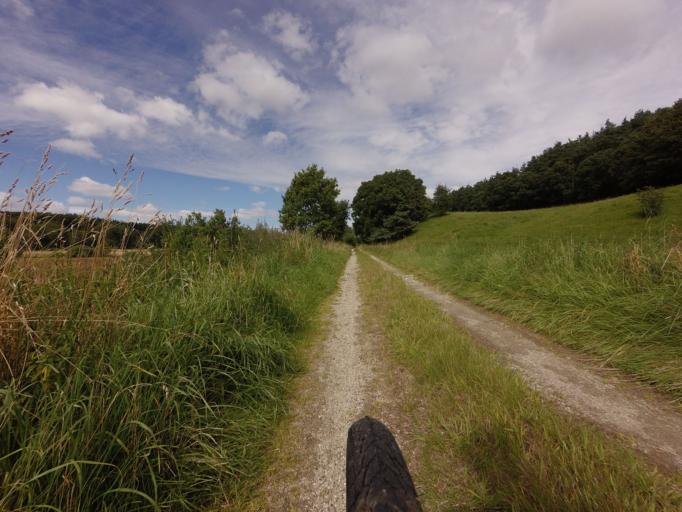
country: DK
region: Central Jutland
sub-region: Syddjurs Kommune
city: Ryomgard
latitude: 56.3916
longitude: 10.5319
